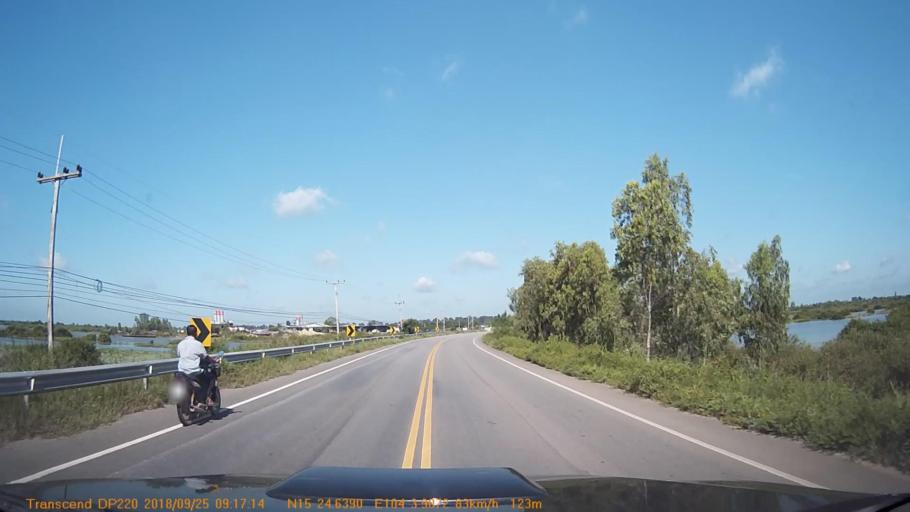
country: TH
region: Sisaket
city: Sila Lat
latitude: 15.4107
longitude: 104.0650
